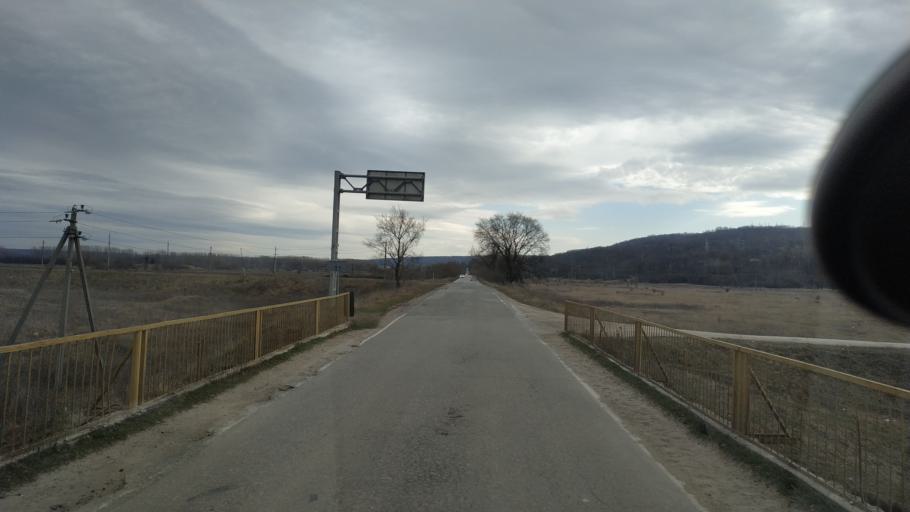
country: MD
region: Chisinau
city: Vadul lui Voda
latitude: 47.1160
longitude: 29.0568
